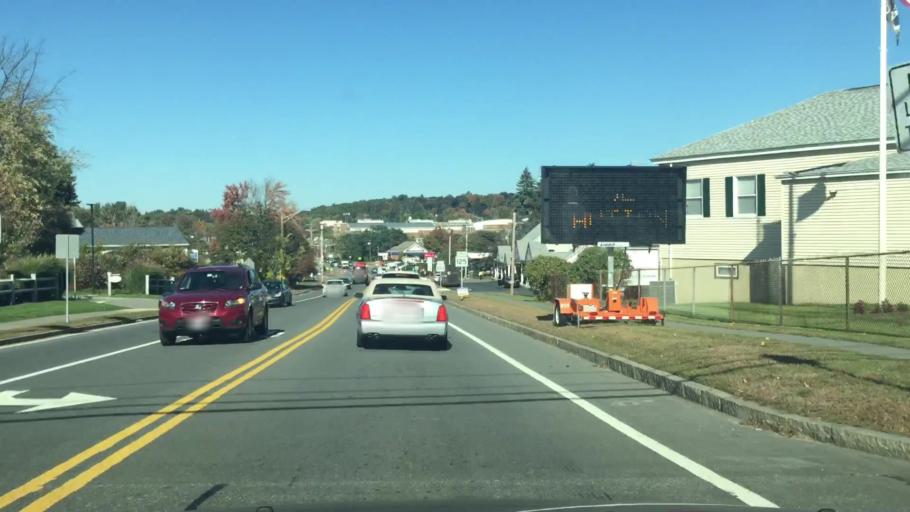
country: US
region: Massachusetts
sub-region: Essex County
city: North Andover
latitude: 42.6938
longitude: -71.1199
